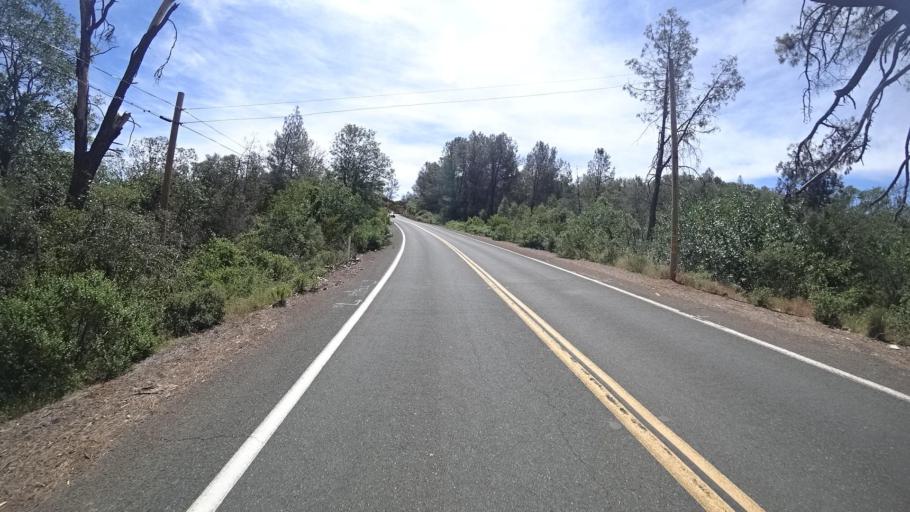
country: US
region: California
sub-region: Lake County
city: Clearlake
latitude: 38.9321
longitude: -122.6588
